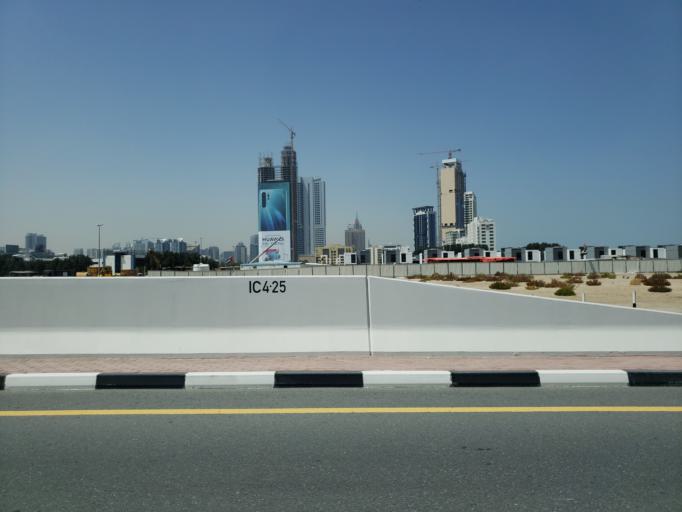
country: AE
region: Dubai
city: Dubai
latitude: 25.1154
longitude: 55.1850
